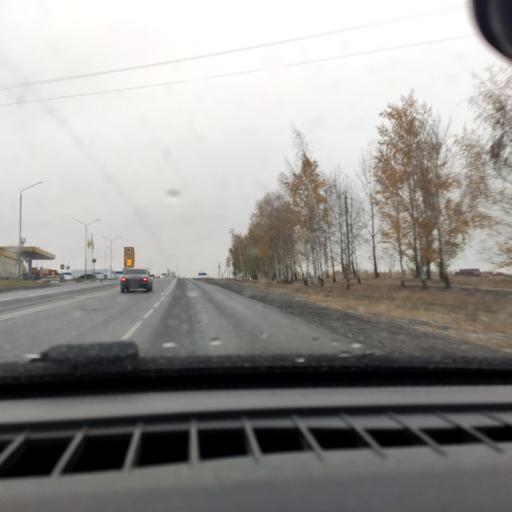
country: RU
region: Belgorod
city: Alekseyevka
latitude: 50.6447
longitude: 38.6815
